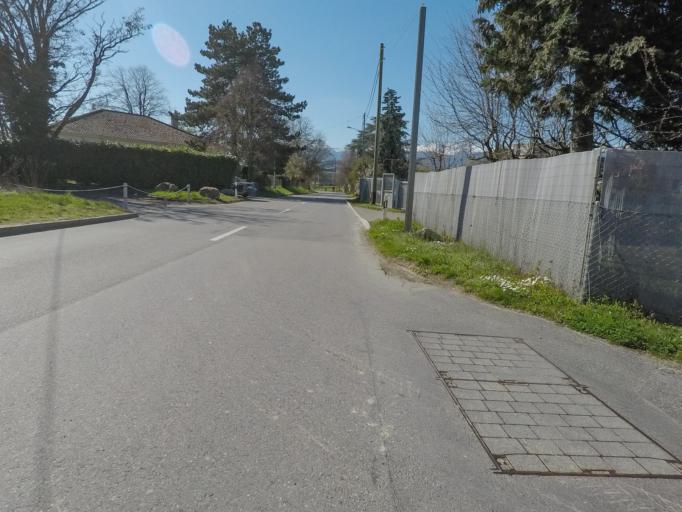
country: CH
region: Geneva
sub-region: Geneva
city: Vernier
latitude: 46.2168
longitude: 6.0787
